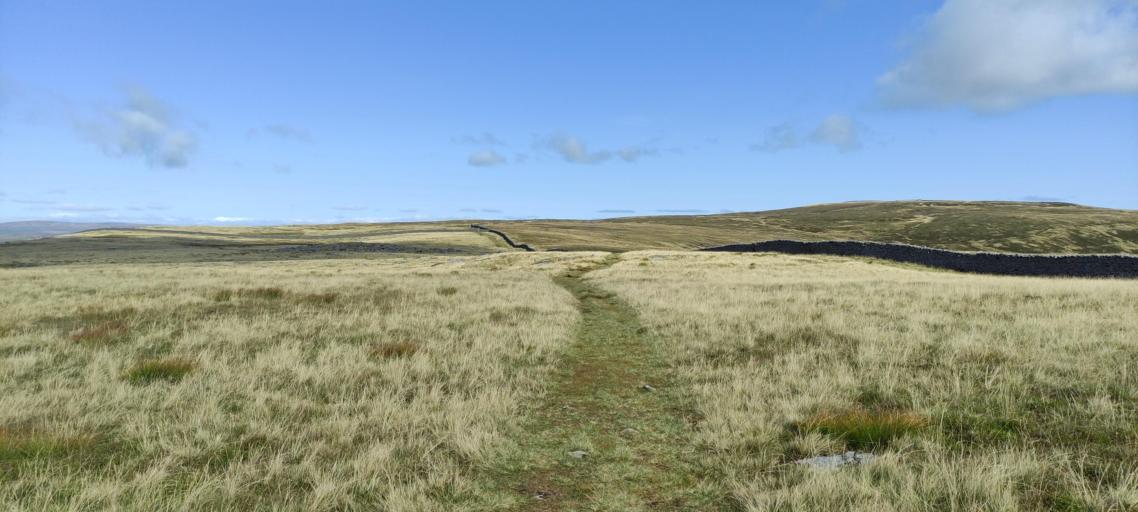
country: GB
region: England
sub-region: North Yorkshire
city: Settle
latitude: 54.1611
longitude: -2.2467
